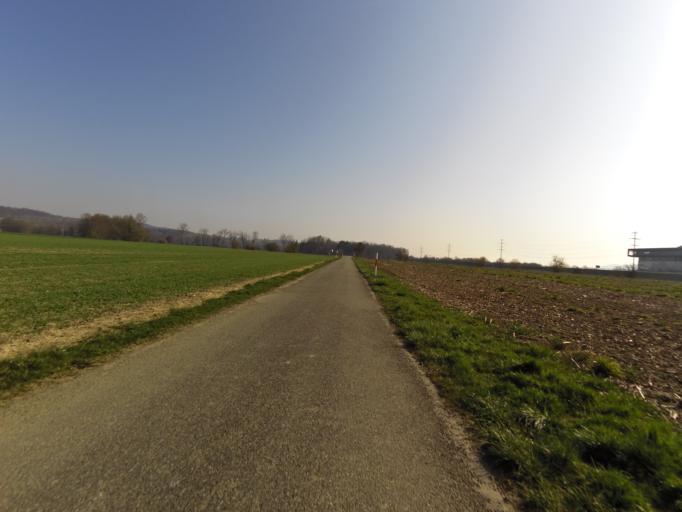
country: CH
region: Thurgau
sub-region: Frauenfeld District
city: Frauenfeld
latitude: 47.5757
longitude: 8.9156
